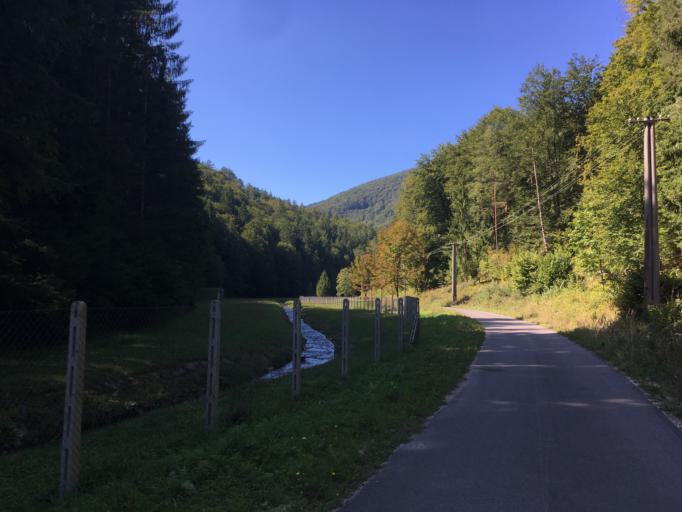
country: SK
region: Trenciansky
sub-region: Okres Povazska Bystrica
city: Povazska Bystrica
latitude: 49.0117
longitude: 18.4477
